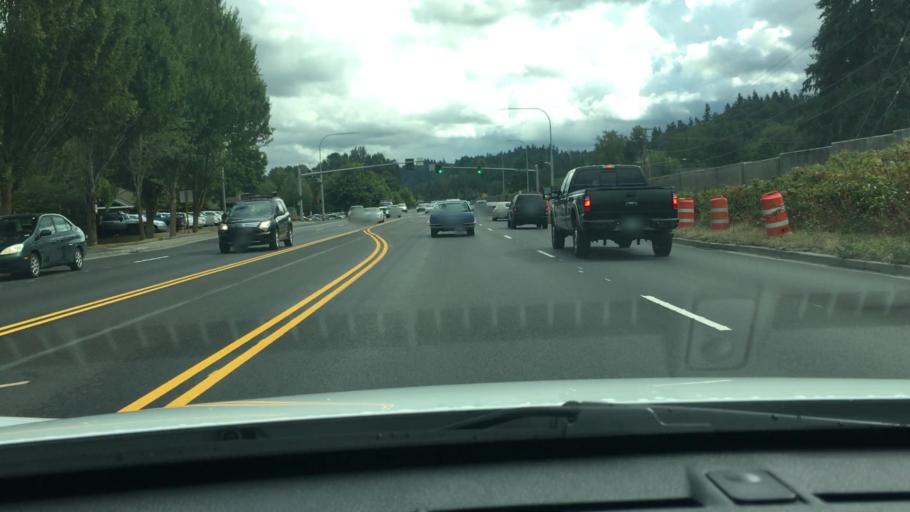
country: US
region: Washington
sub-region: King County
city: Fairwood
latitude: 47.4714
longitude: -122.1645
